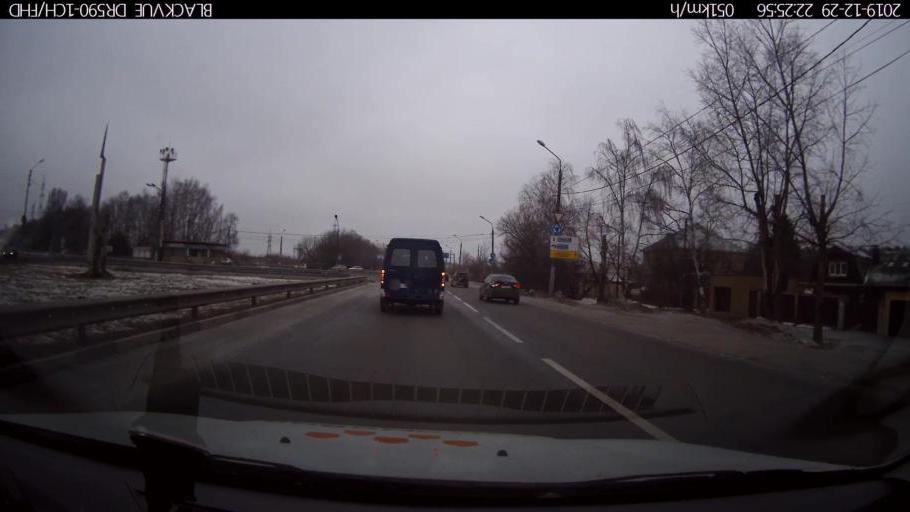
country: RU
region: Nizjnij Novgorod
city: Nizhniy Novgorod
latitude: 56.2149
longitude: 43.9292
